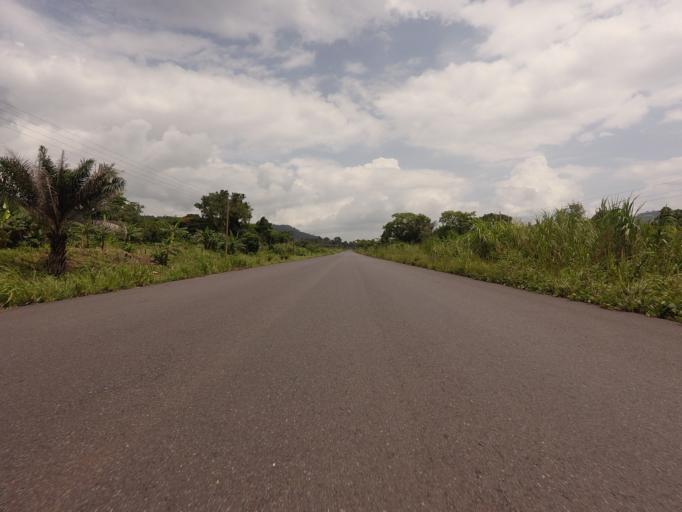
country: GH
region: Volta
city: Ho
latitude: 6.5501
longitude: 0.2549
